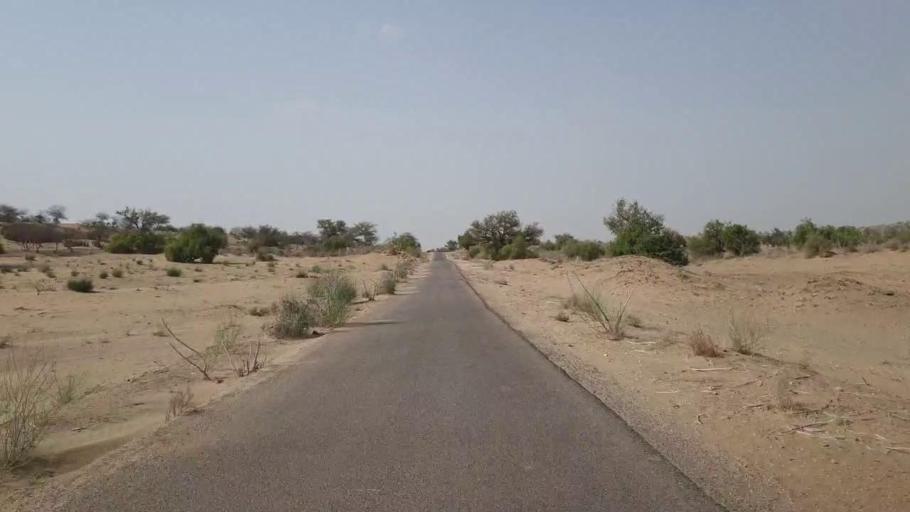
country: PK
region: Sindh
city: Mithi
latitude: 24.5912
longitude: 69.9238
